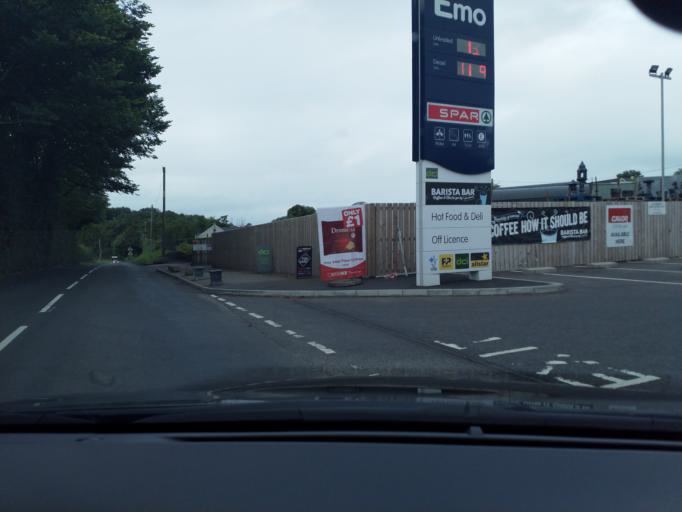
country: GB
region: Northern Ireland
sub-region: Dungannon District
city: Dungannon
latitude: 54.4456
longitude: -6.7952
